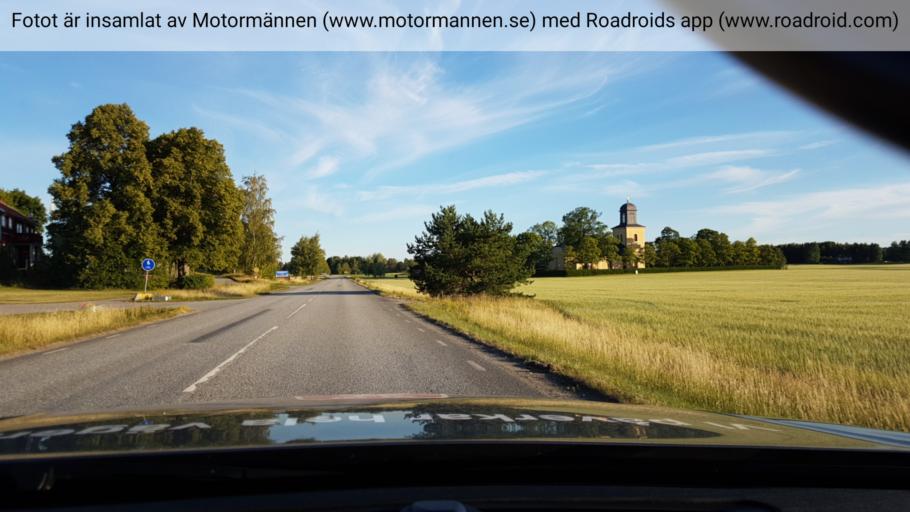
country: SE
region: Vaestmanland
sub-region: Vasteras
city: Skultuna
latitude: 59.7741
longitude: 16.4613
